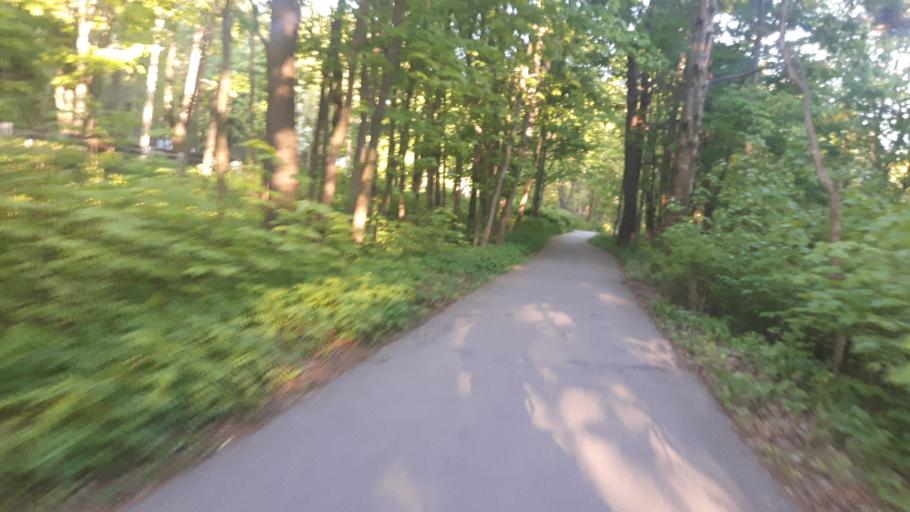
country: RU
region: Leningrad
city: Roshchino
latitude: 60.1946
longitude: 29.6238
